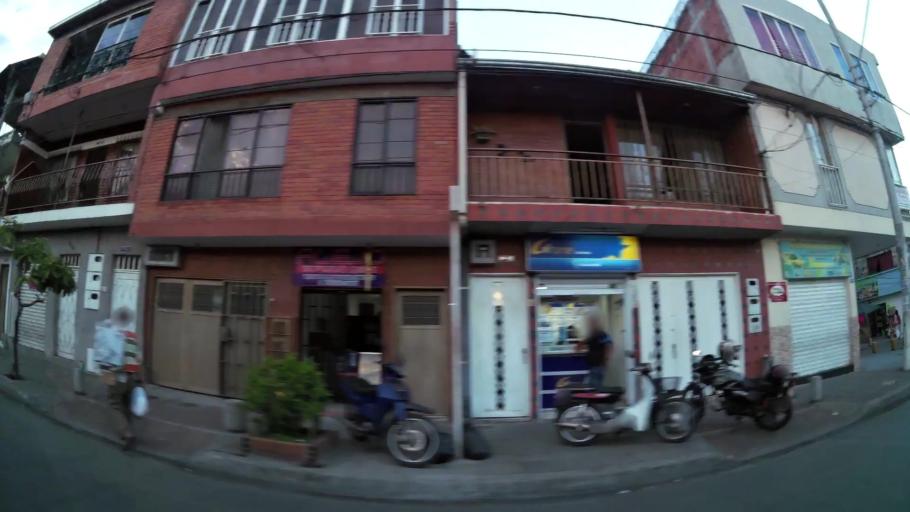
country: CO
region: Valle del Cauca
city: Cali
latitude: 3.4445
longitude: -76.5025
